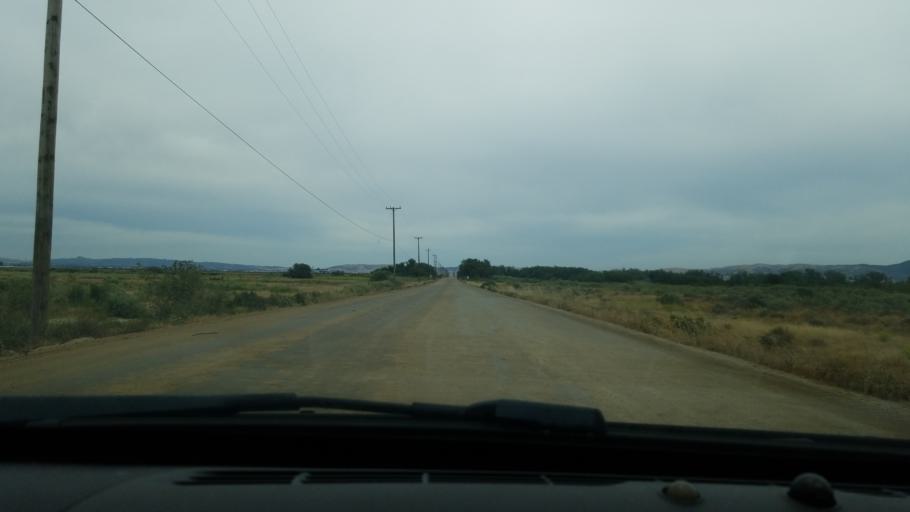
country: US
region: California
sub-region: Santa Barbara County
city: Guadalupe
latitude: 34.9853
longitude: -120.5135
